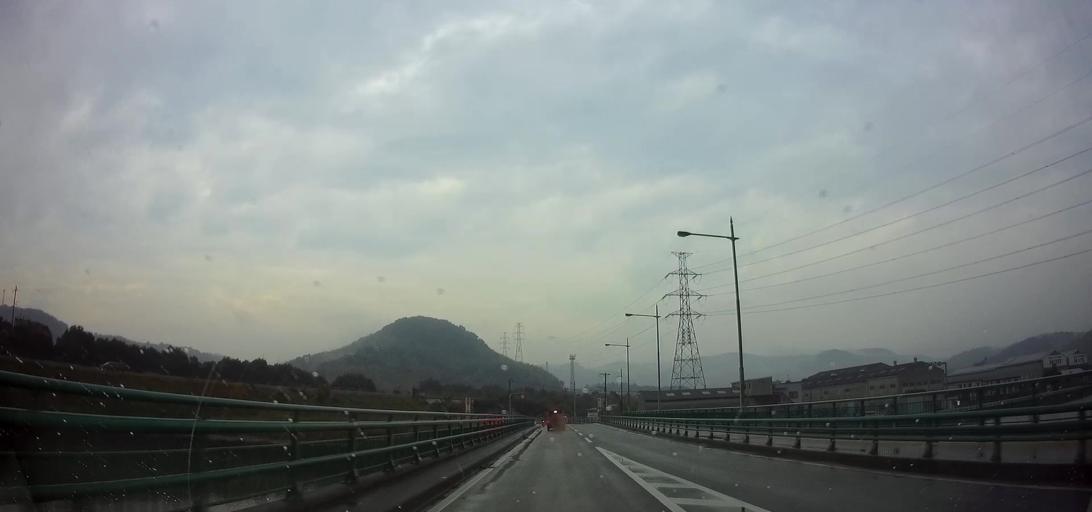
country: JP
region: Nagasaki
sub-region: Isahaya-shi
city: Isahaya
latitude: 32.8480
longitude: 130.0107
